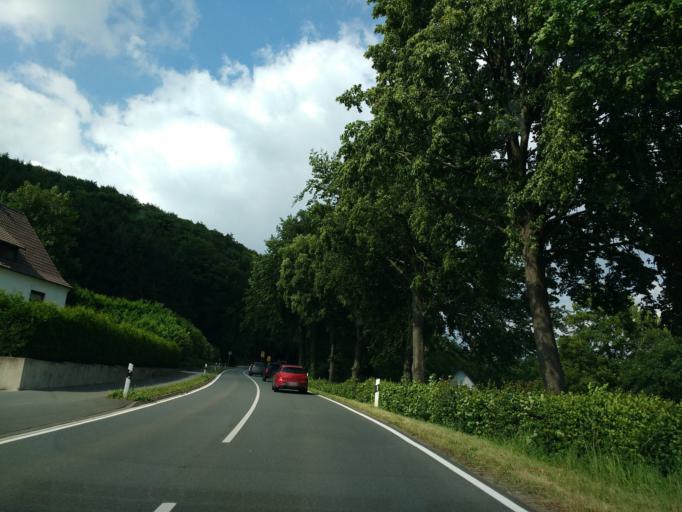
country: DE
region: North Rhine-Westphalia
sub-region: Regierungsbezirk Detmold
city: Lemgo
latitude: 52.0820
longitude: 8.9315
